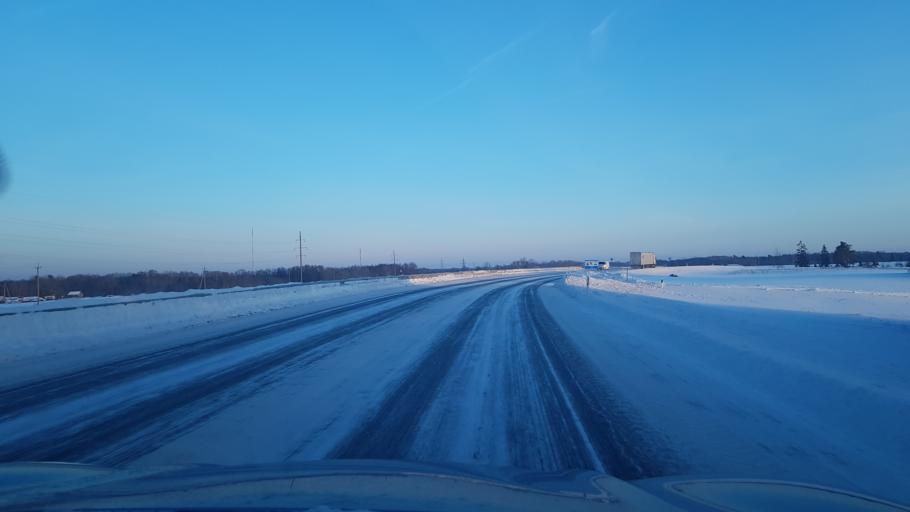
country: EE
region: Ida-Virumaa
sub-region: Narva-Joesuu linn
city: Narva-Joesuu
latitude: 59.4045
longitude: 28.0489
